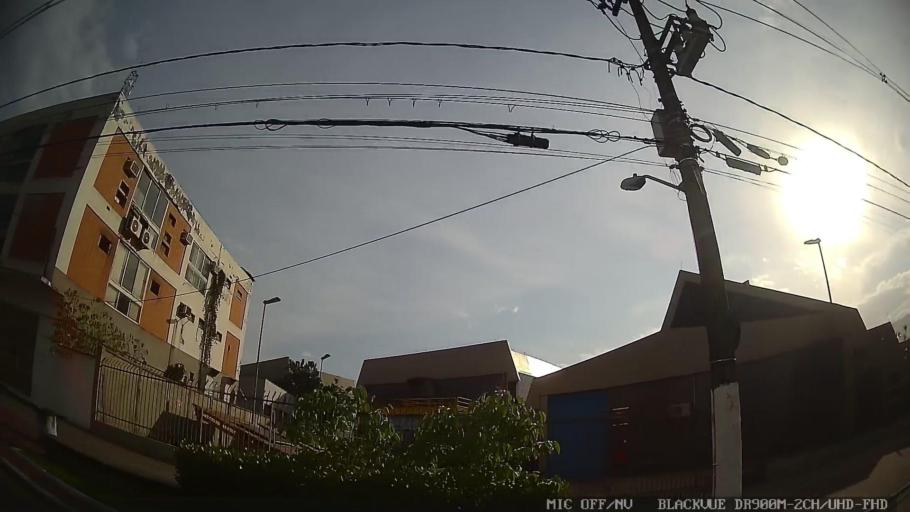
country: BR
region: Sao Paulo
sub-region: Cubatao
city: Cubatao
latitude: -23.8824
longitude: -46.4213
